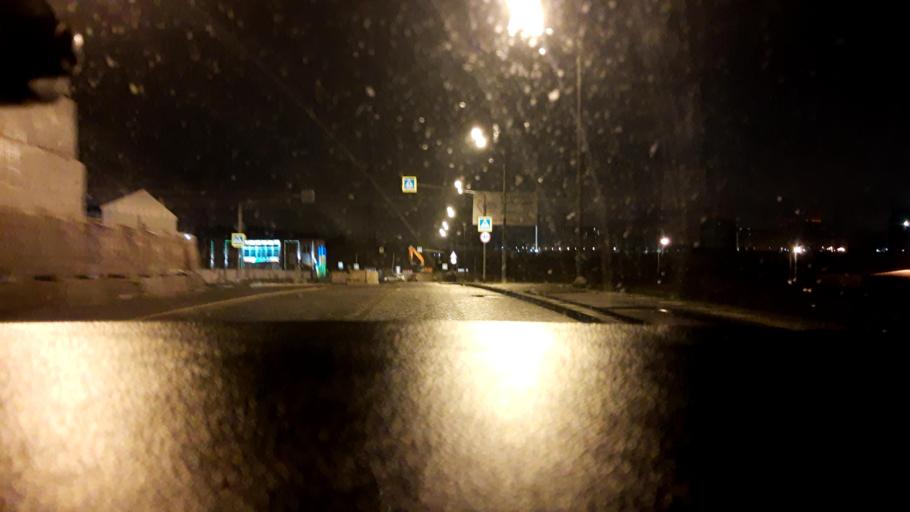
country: RU
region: Moskovskaya
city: Pavshino
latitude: 55.8646
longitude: 37.3655
